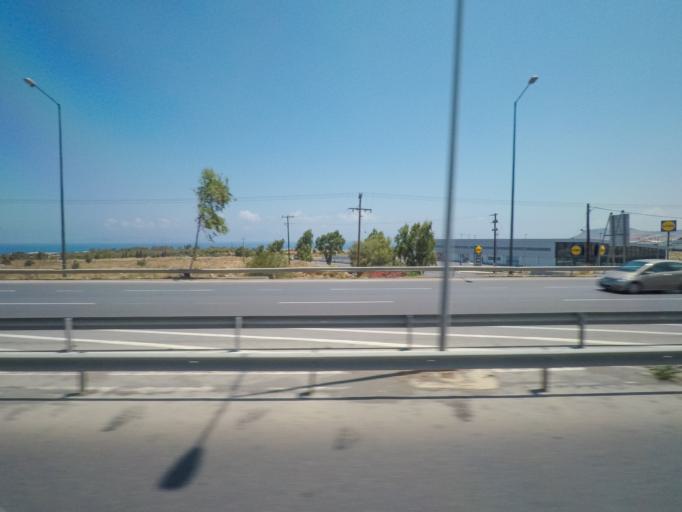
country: GR
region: Crete
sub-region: Nomos Irakleiou
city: Nea Alikarnassos
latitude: 35.3269
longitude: 25.1782
